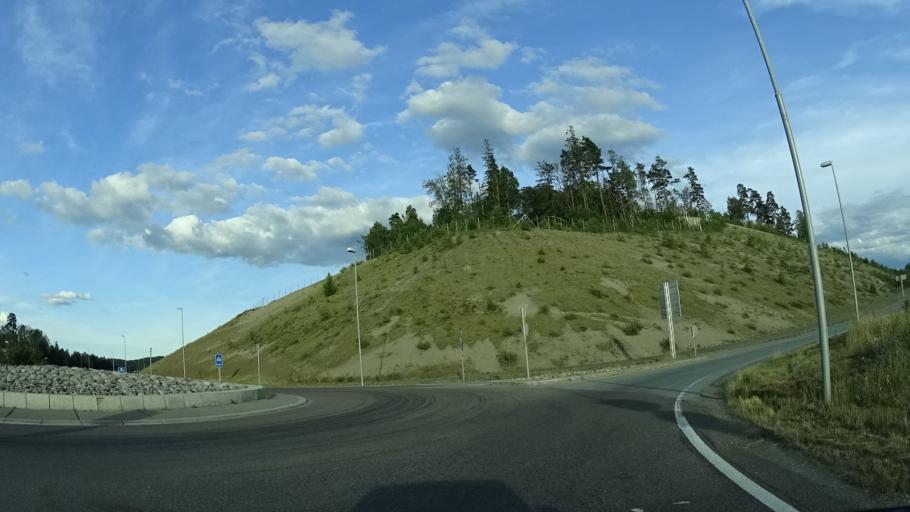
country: NO
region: Ostfold
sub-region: Eidsberg
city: Mysen
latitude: 59.5762
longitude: 11.3247
